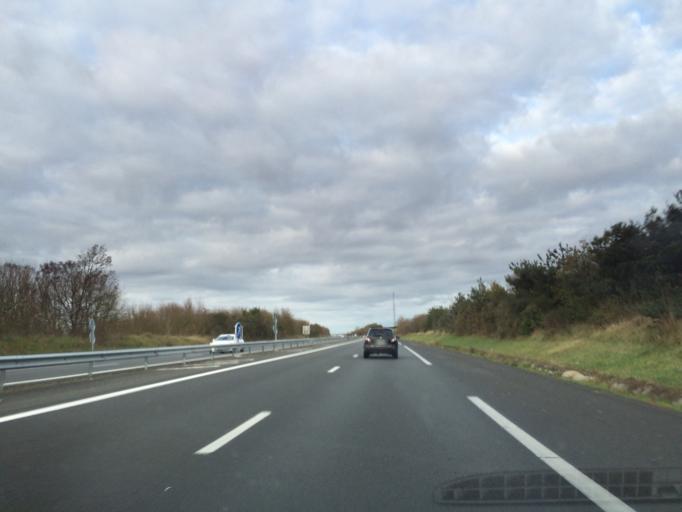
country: FR
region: Poitou-Charentes
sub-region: Departement de la Charente-Maritime
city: Saint-Jean-d'Angely
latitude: 46.0341
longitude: -0.5373
